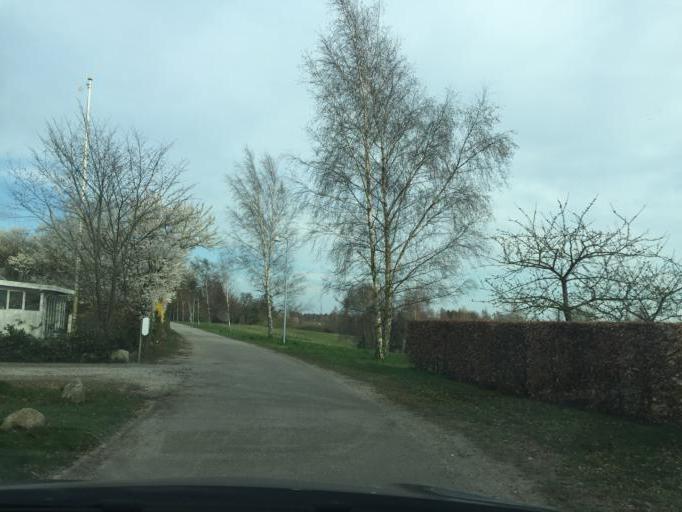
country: DK
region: South Denmark
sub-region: Faaborg-Midtfyn Kommune
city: Arslev
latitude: 55.3222
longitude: 10.5133
